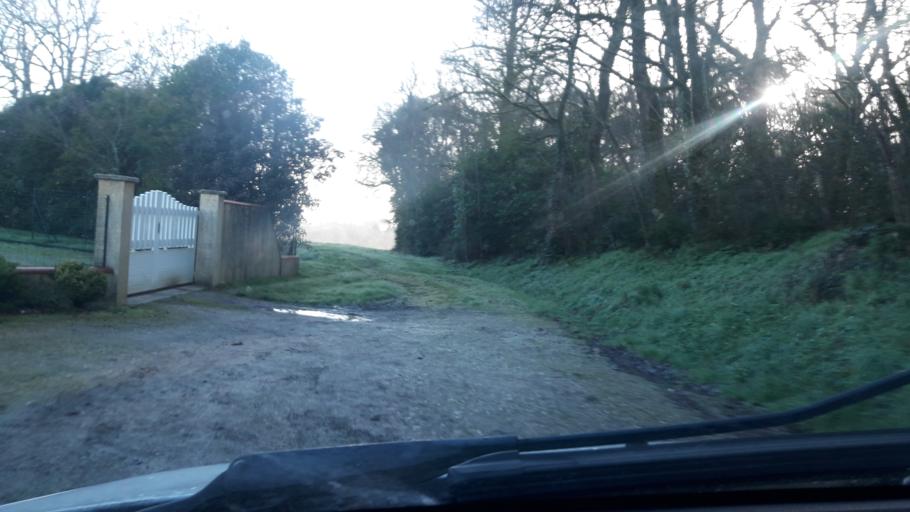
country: FR
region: Midi-Pyrenees
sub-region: Departement du Gers
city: Gimont
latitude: 43.6433
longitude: 0.9989
